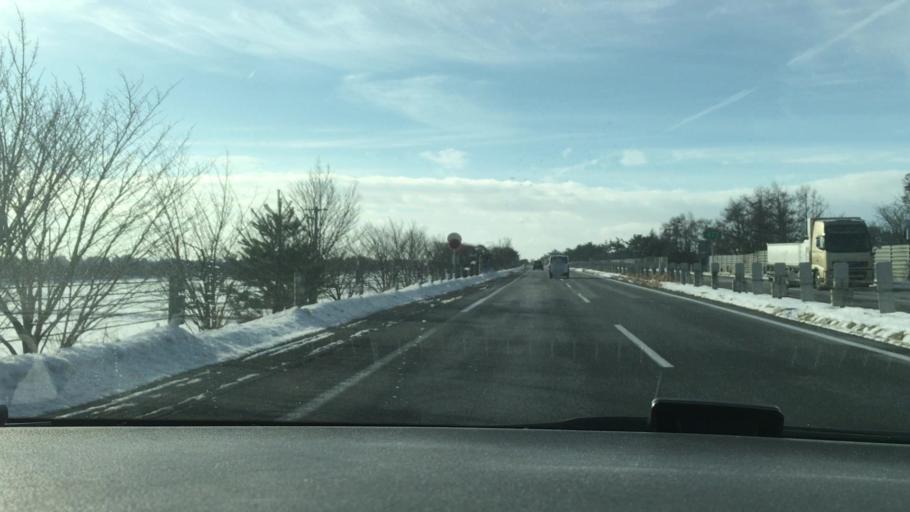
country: JP
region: Iwate
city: Hanamaki
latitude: 39.3650
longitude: 141.0913
